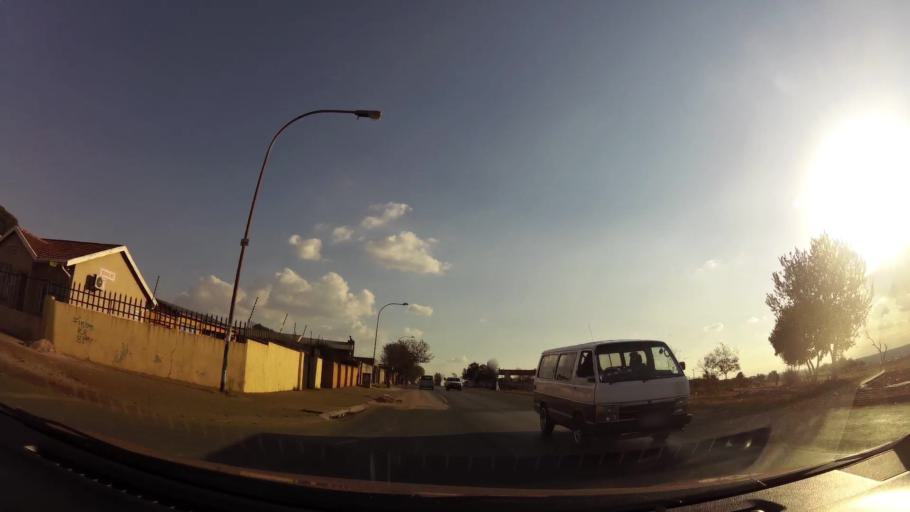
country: ZA
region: Gauteng
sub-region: City of Johannesburg Metropolitan Municipality
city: Soweto
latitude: -26.2269
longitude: 27.8547
